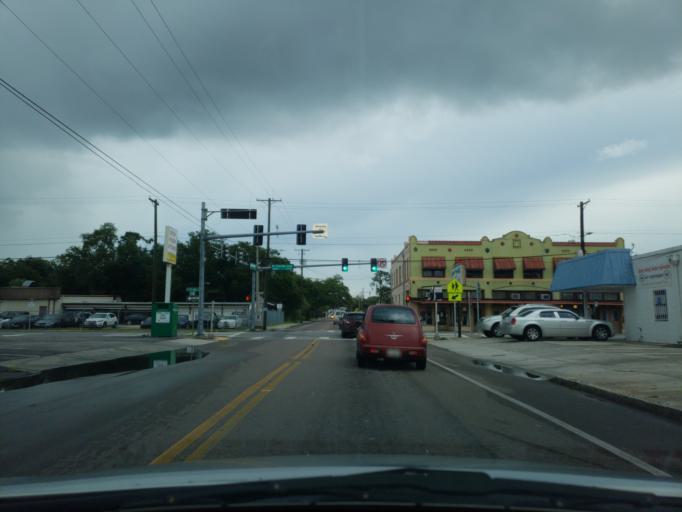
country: US
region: Florida
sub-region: Hillsborough County
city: Tampa
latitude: 27.9888
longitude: -82.4599
